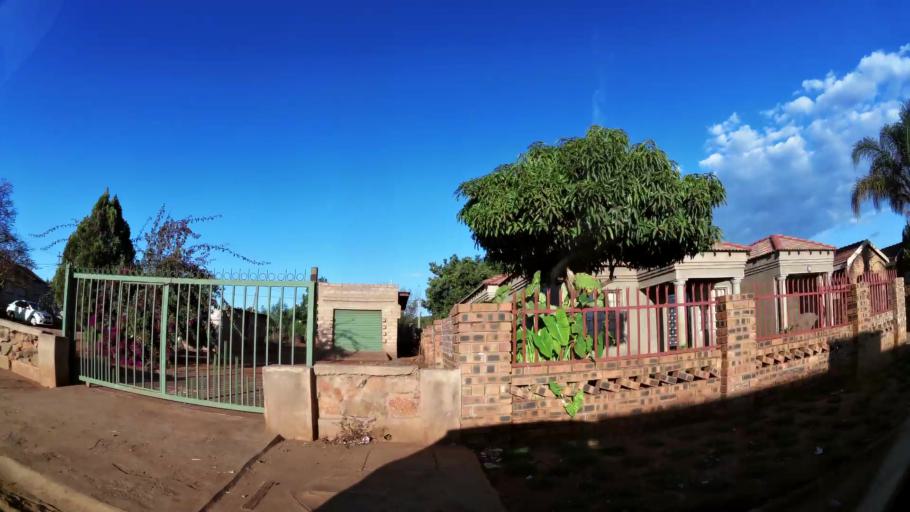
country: ZA
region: Limpopo
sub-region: Waterberg District Municipality
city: Mokopane
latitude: -24.1535
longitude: 28.9935
